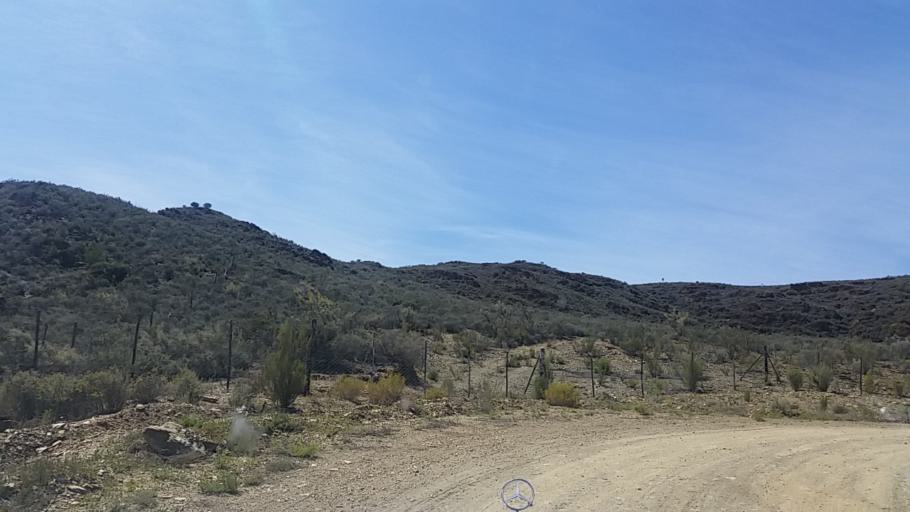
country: ZA
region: Western Cape
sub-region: Eden District Municipality
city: Knysna
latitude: -33.6482
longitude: 23.1380
